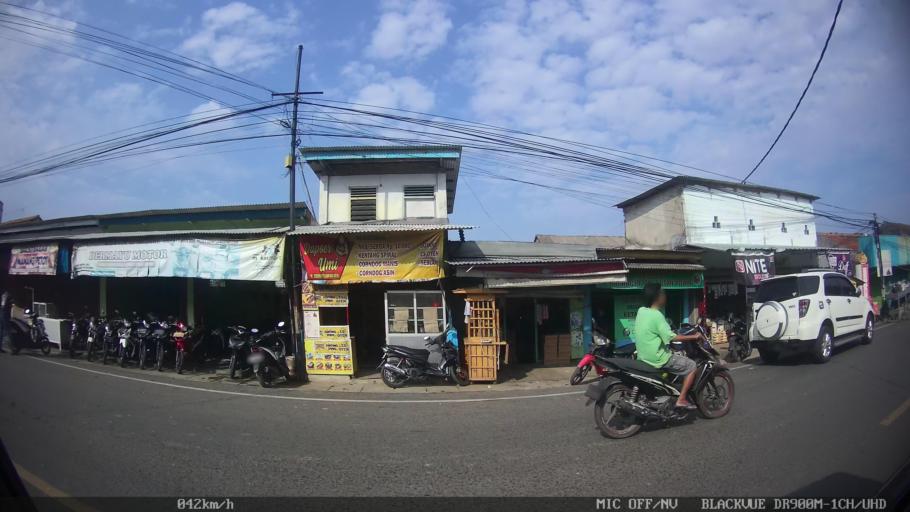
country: ID
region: Lampung
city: Panjang
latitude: -5.4790
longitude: 105.3236
